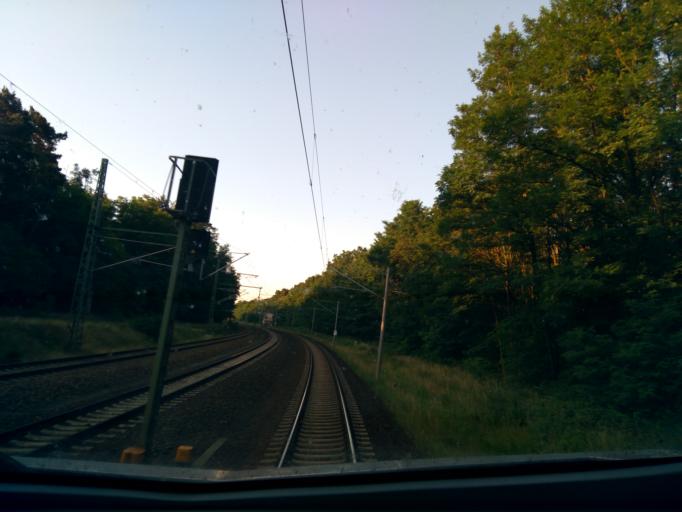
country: DE
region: Brandenburg
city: Halbe
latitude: 52.0352
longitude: 13.7186
